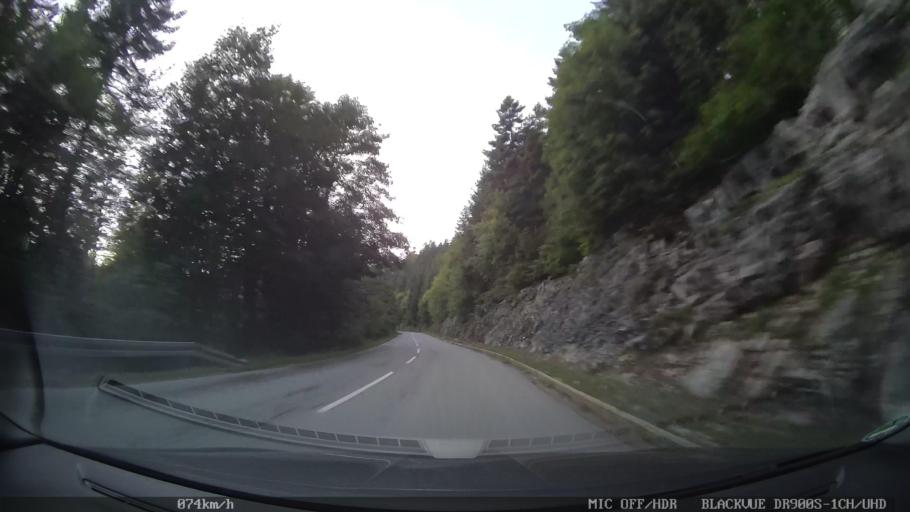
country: HR
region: Primorsko-Goranska
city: Novi Vinodolski
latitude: 45.1857
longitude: 14.9239
